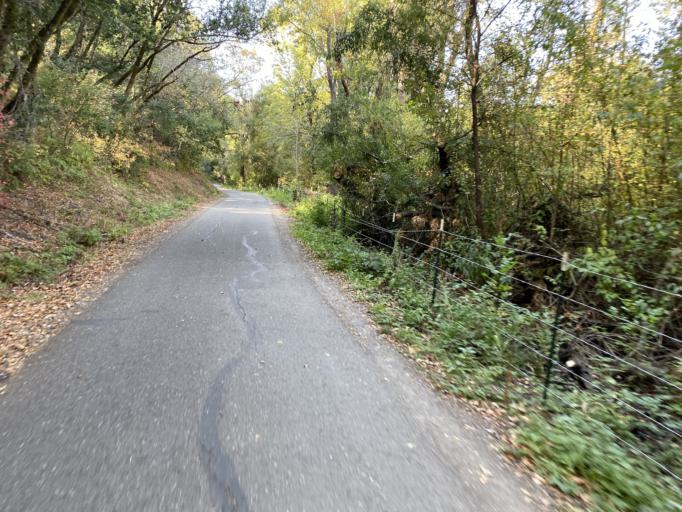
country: US
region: California
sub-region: San Mateo County
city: Hillsborough
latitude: 37.5634
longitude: -122.3979
